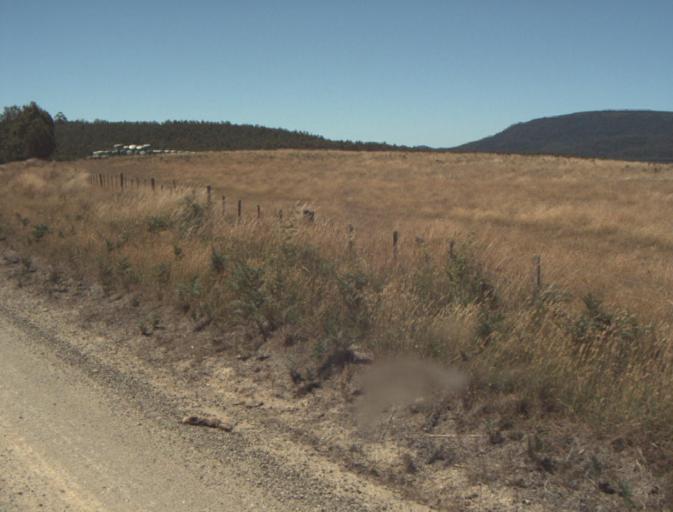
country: AU
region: Tasmania
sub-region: Dorset
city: Scottsdale
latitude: -41.3255
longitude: 147.4448
